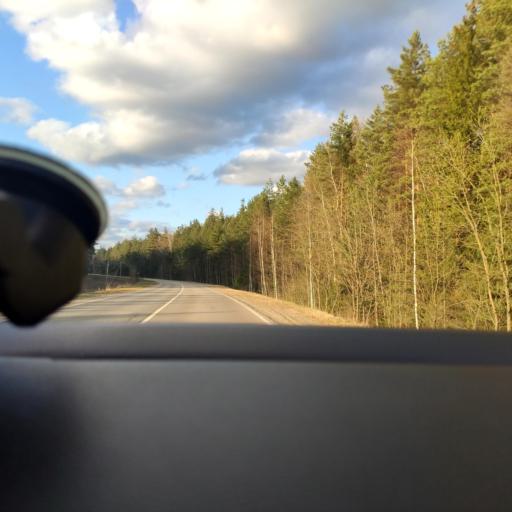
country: RU
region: Moskovskaya
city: Shaturtorf
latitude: 55.4378
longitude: 39.4306
